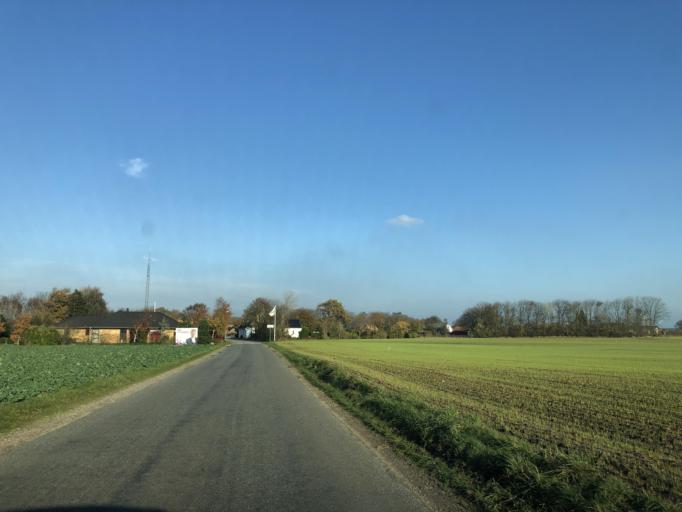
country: DK
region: Central Jutland
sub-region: Holstebro Kommune
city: Vinderup
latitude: 56.4004
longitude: 8.7493
